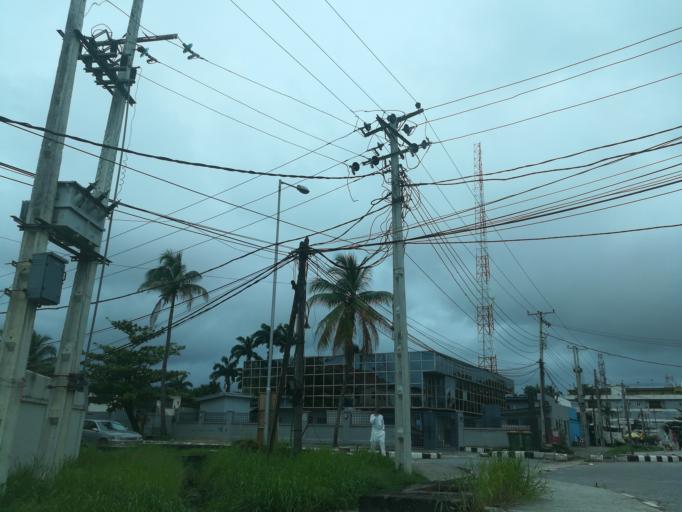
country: NG
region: Lagos
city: Ikoyi
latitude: 6.4255
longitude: 3.4192
